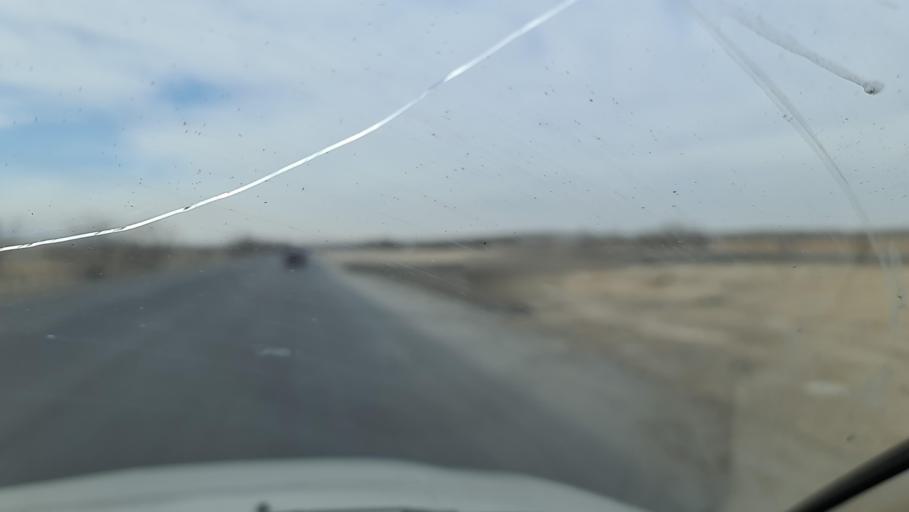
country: KG
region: Chuy
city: Bystrovka
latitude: 43.3205
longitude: 76.0168
